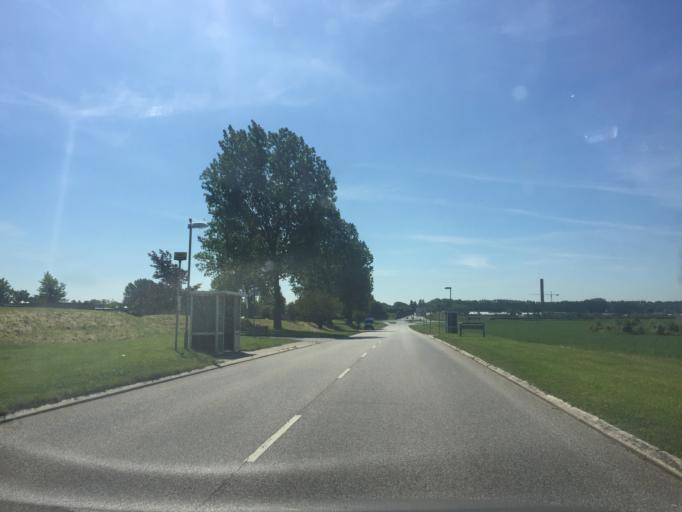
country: DK
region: Capital Region
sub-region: Hoje-Taastrup Kommune
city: Flong
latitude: 55.6596
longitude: 12.1757
